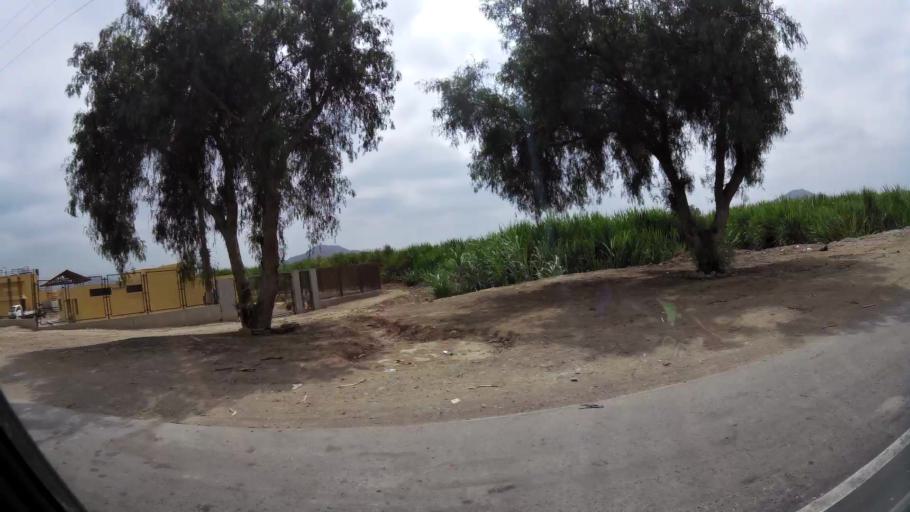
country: PE
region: La Libertad
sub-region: Ascope
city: Chocope
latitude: -7.7910
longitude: -79.2281
